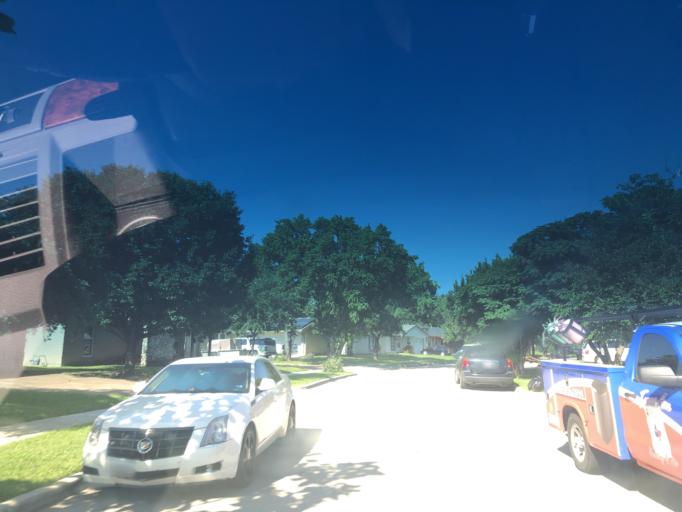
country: US
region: Texas
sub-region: Dallas County
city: Grand Prairie
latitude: 32.7141
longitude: -97.0086
